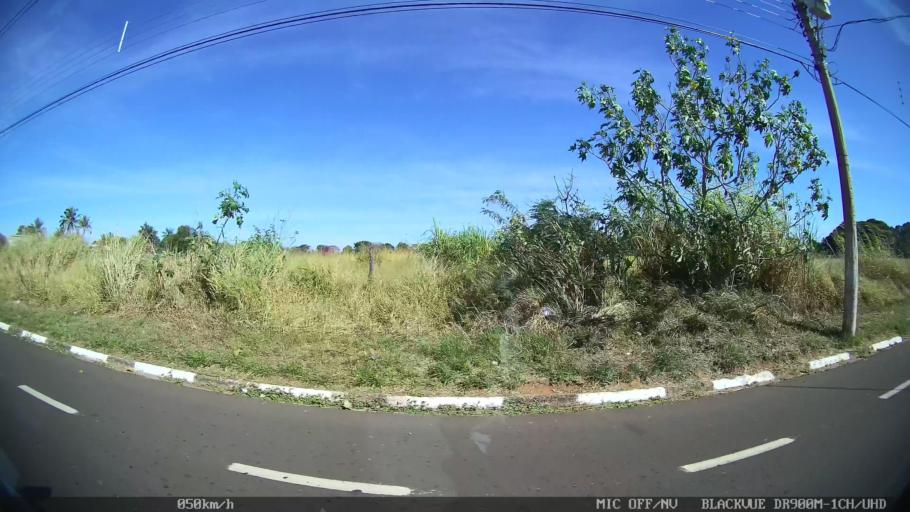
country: BR
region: Sao Paulo
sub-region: Franca
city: Franca
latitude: -20.5620
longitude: -47.3590
